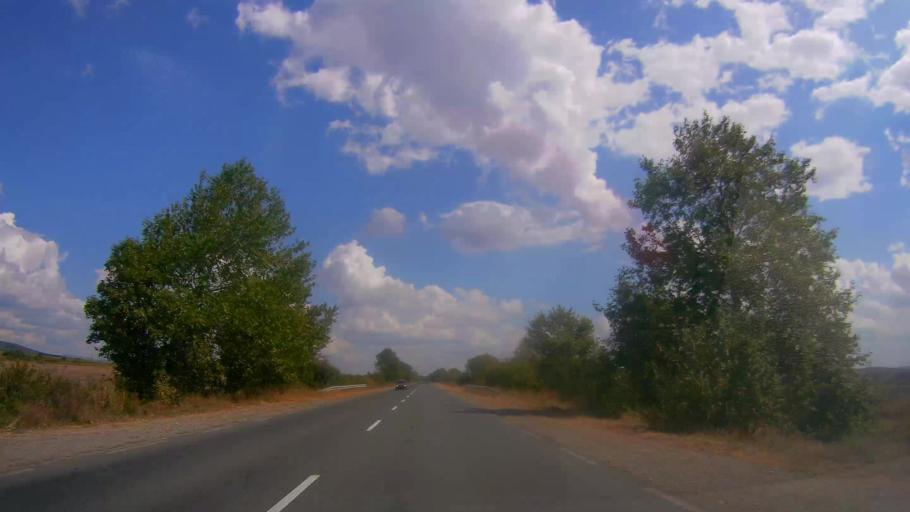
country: BG
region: Sliven
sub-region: Obshtina Sliven
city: Kermen
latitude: 42.6343
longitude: 26.1626
